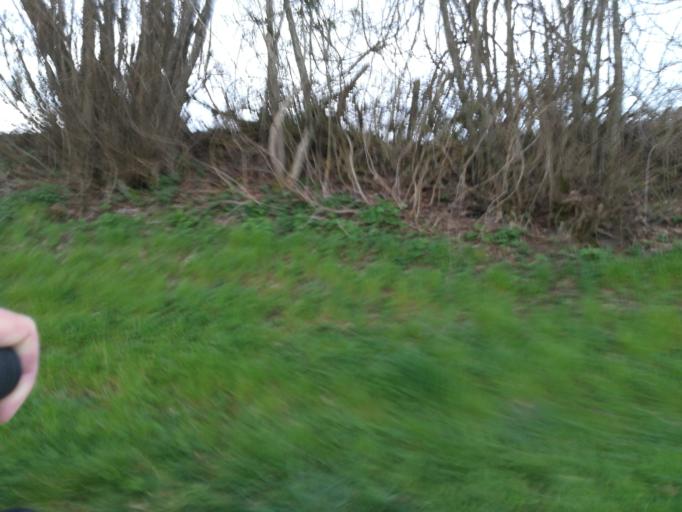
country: DE
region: Baden-Wuerttemberg
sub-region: Freiburg Region
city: Volkertshausen
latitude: 47.7830
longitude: 8.8682
